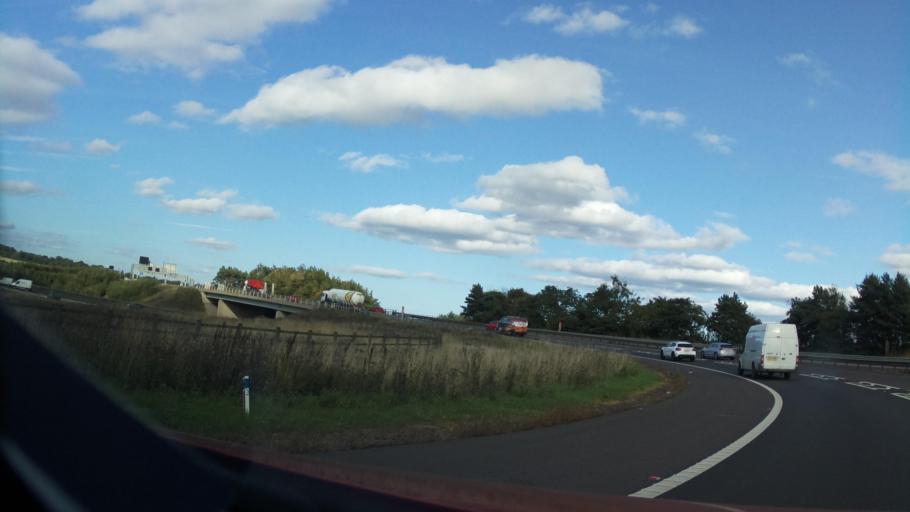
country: GB
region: Scotland
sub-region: Edinburgh
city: Kirkliston
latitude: 55.9535
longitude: -3.4211
